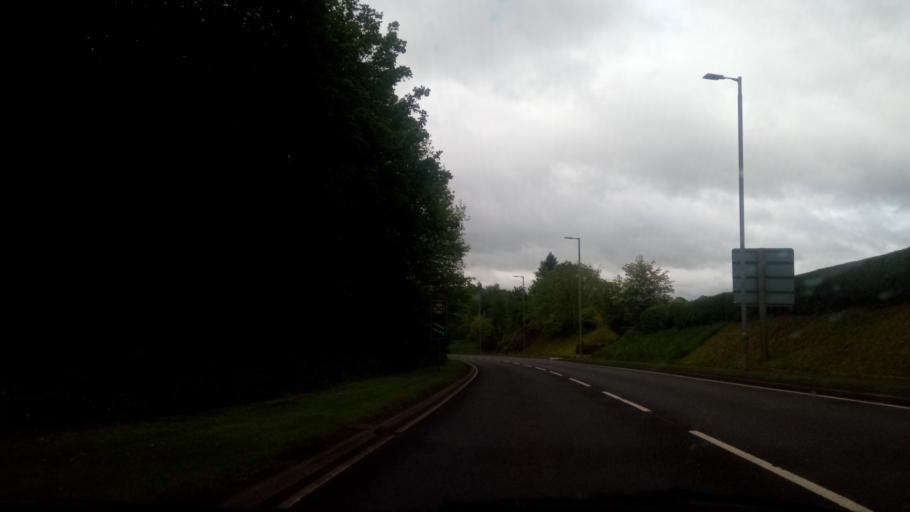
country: GB
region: Scotland
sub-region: The Scottish Borders
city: Hawick
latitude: 55.4369
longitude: -2.7791
